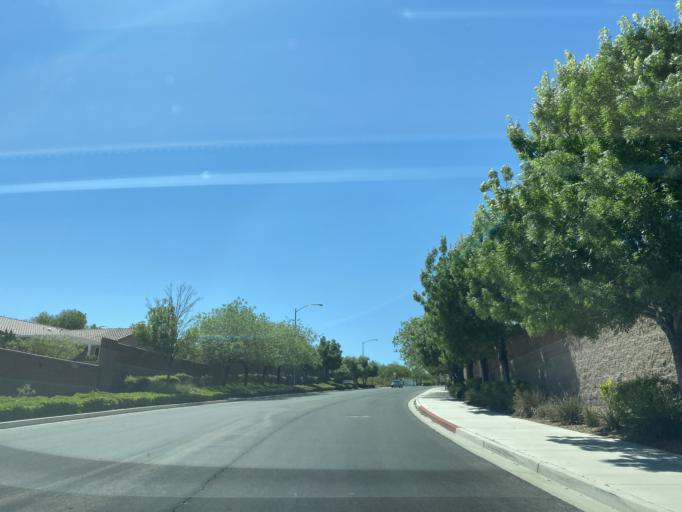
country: US
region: Nevada
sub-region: Clark County
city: Whitney
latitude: 35.9472
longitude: -115.0845
